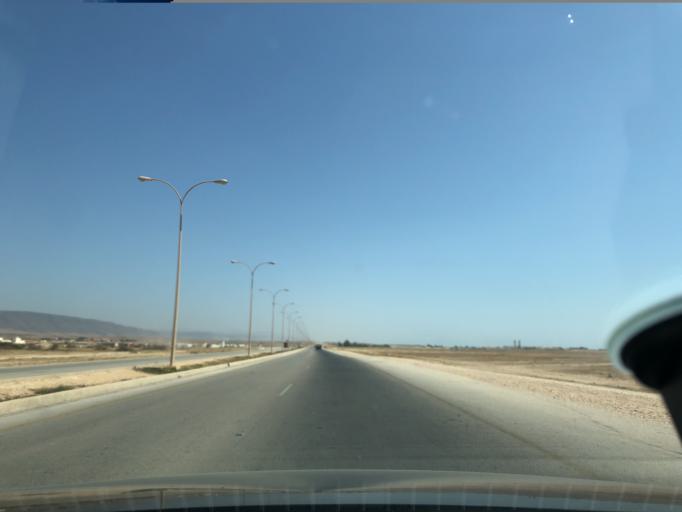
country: OM
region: Zufar
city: Salalah
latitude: 17.0530
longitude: 54.2827
